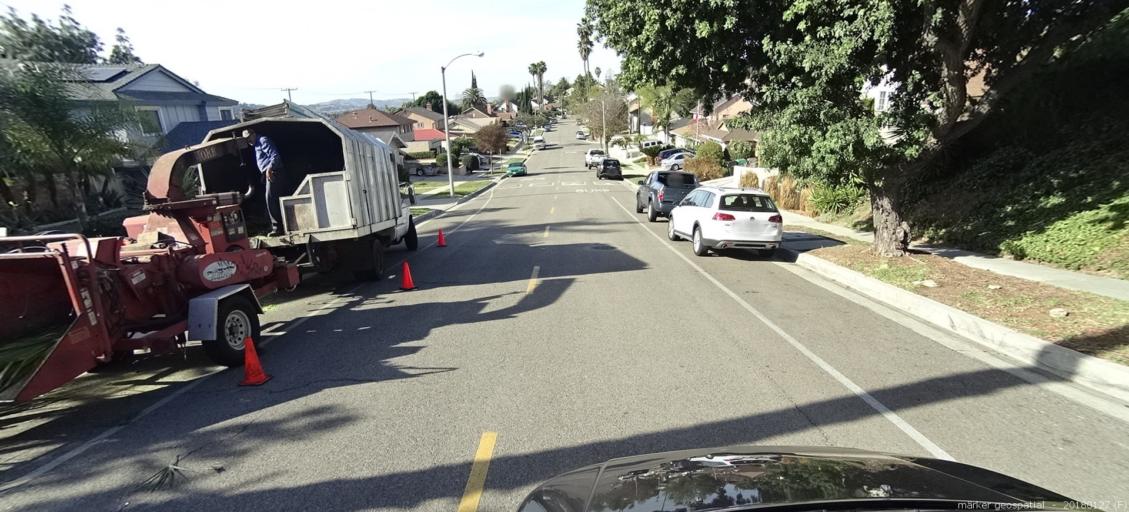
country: US
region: California
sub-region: Los Angeles County
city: Diamond Bar
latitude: 34.0282
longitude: -117.8000
